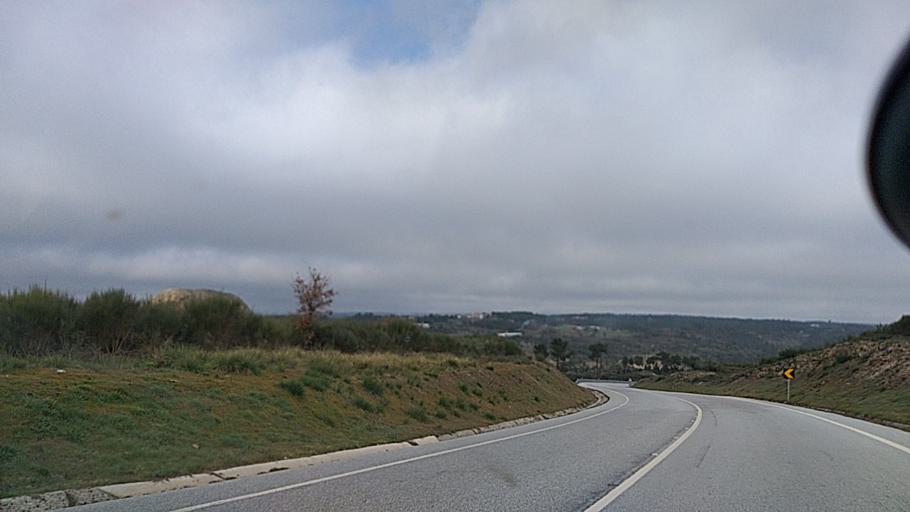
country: PT
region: Guarda
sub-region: Aguiar da Beira
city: Aguiar da Beira
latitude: 40.7707
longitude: -7.5035
